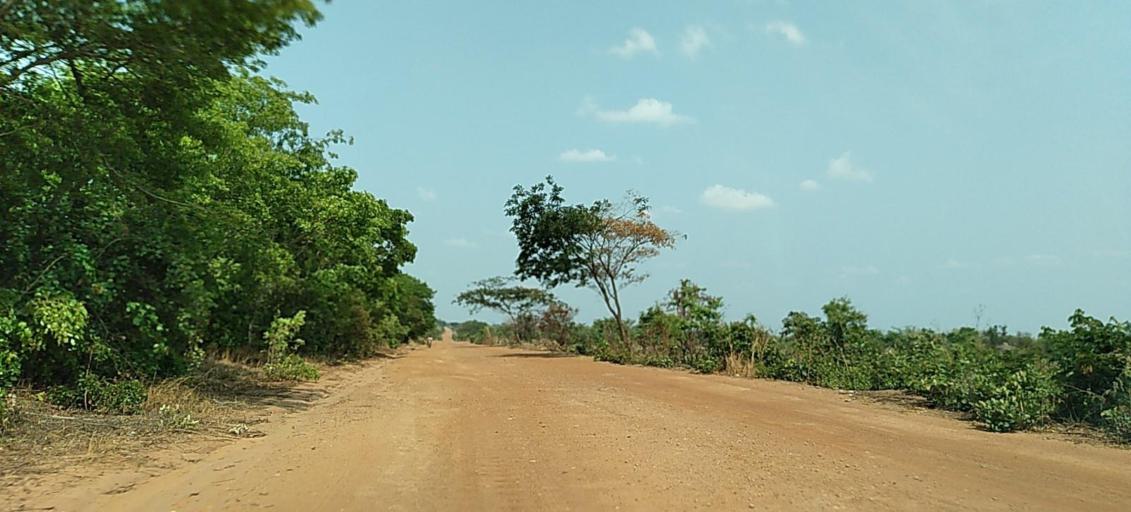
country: ZM
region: Copperbelt
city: Luanshya
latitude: -13.0921
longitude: 28.3010
